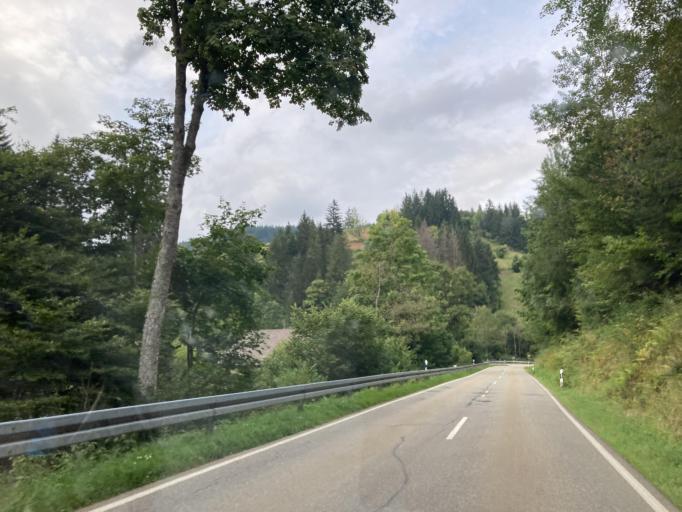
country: DE
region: Baden-Wuerttemberg
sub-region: Freiburg Region
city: Bollen
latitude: 47.7875
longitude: 7.8555
